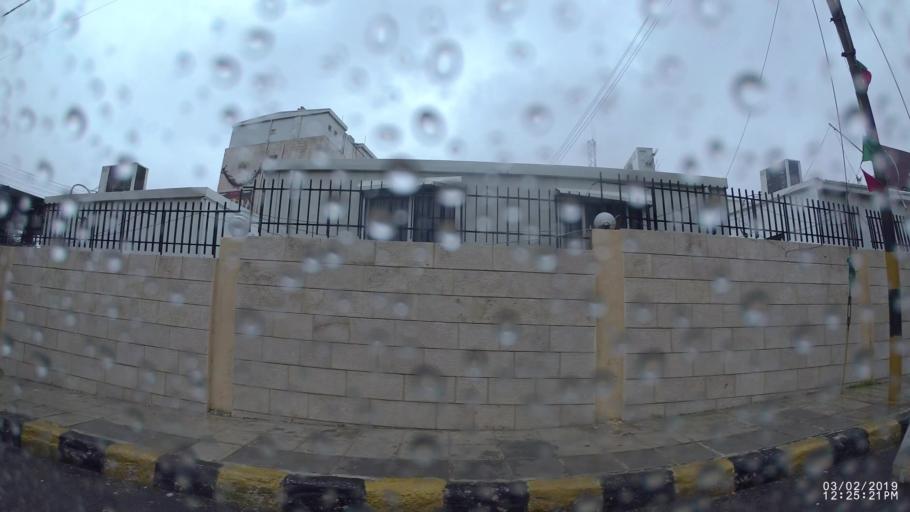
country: JO
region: Amman
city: Amman
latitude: 31.9589
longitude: 35.9110
